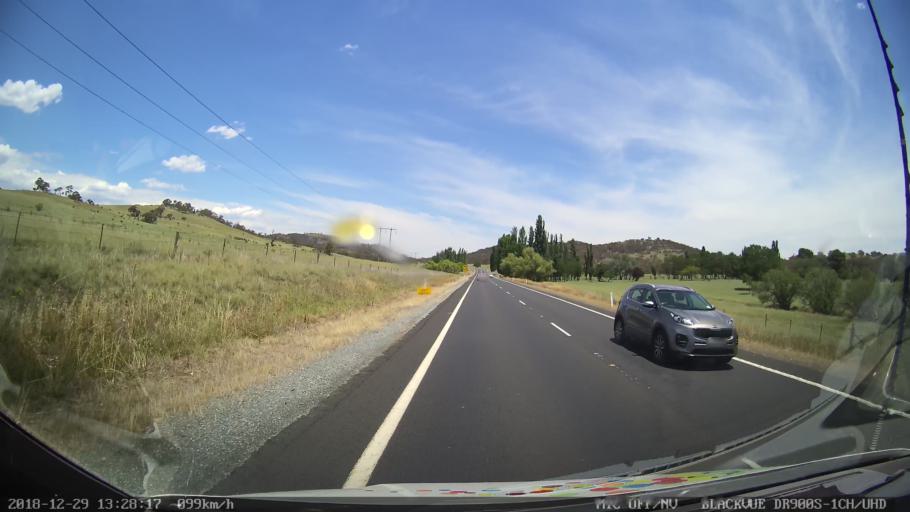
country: AU
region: New South Wales
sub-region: Cooma-Monaro
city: Cooma
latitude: -35.8735
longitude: 149.1615
